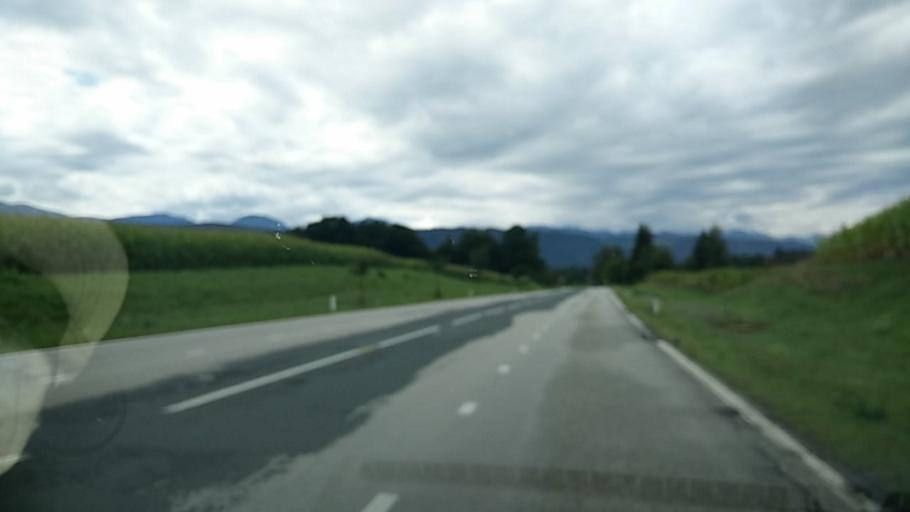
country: AT
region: Carinthia
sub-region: Politischer Bezirk Klagenfurt Land
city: Poggersdorf
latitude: 46.6360
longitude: 14.4215
